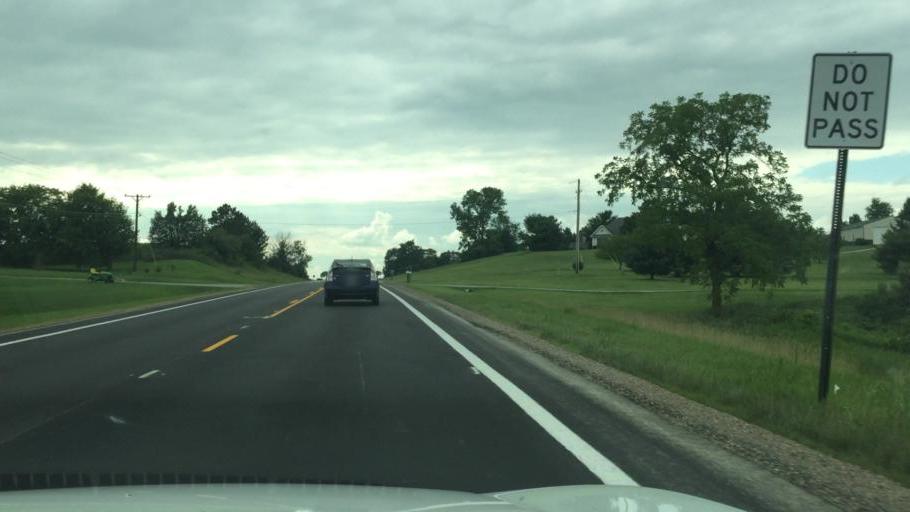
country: US
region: Ohio
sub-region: Champaign County
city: Urbana
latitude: 40.0833
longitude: -83.6622
